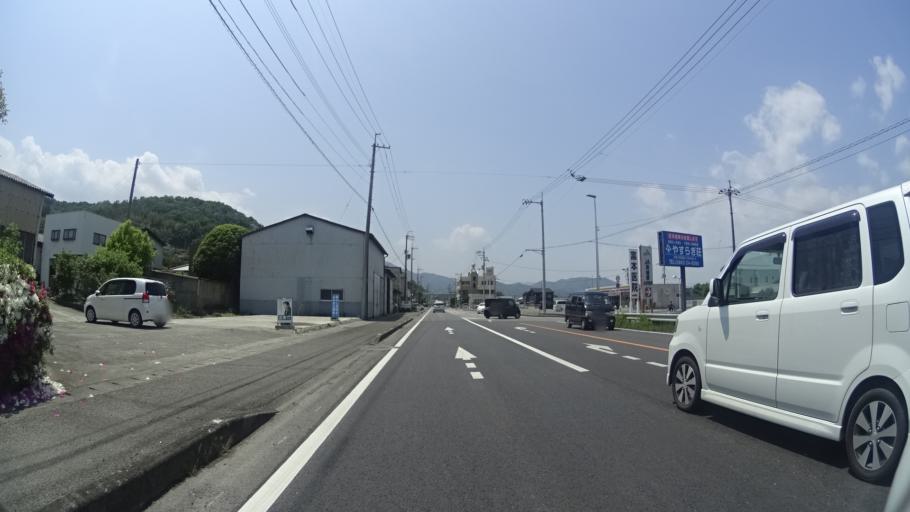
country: JP
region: Tokushima
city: Kamojimacho-jogejima
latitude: 34.0610
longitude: 134.2542
